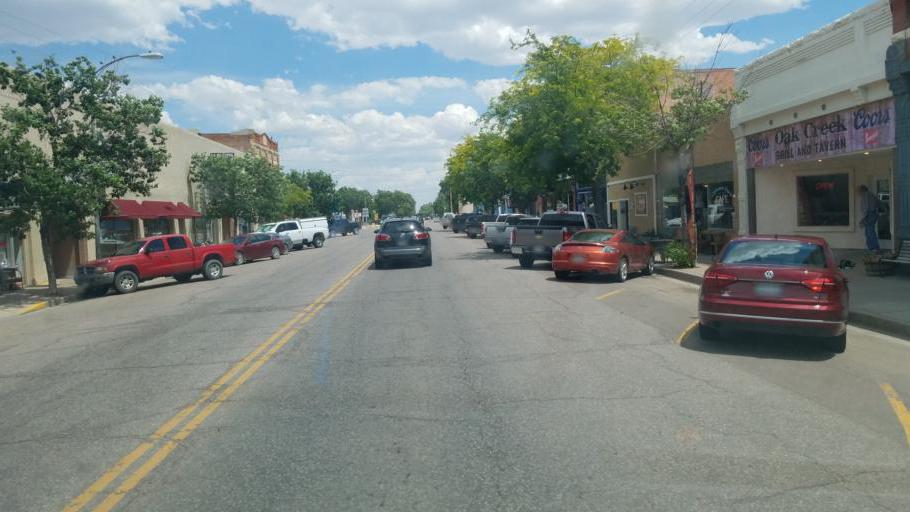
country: US
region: Colorado
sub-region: Fremont County
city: Florence
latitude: 38.3898
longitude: -105.1172
